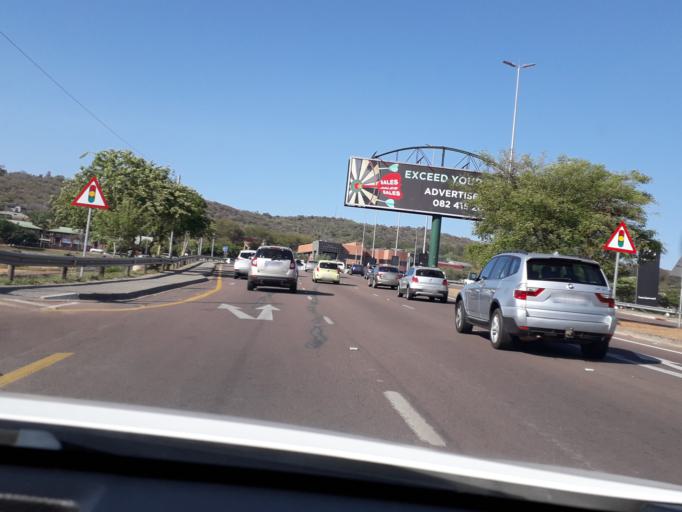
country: ZA
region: Gauteng
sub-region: City of Tshwane Metropolitan Municipality
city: Pretoria
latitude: -25.7654
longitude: 28.3222
